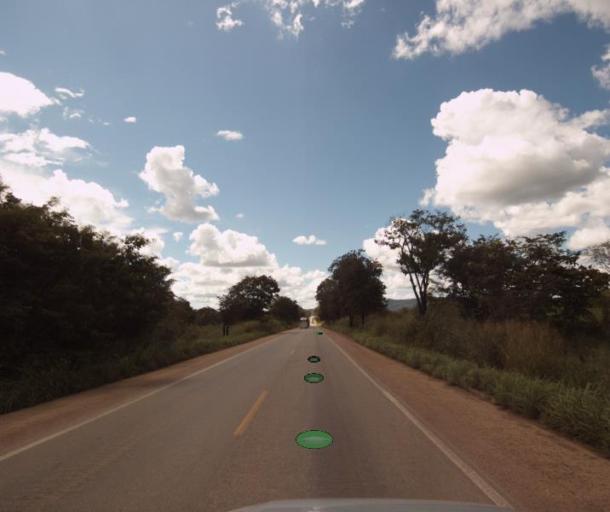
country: BR
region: Goias
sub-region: Porangatu
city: Porangatu
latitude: -13.7014
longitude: -49.0214
